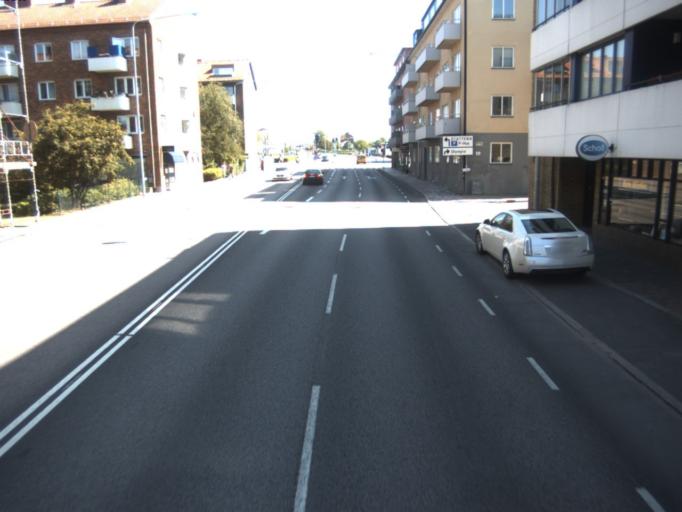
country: SE
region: Skane
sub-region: Helsingborg
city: Helsingborg
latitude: 56.0557
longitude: 12.6997
